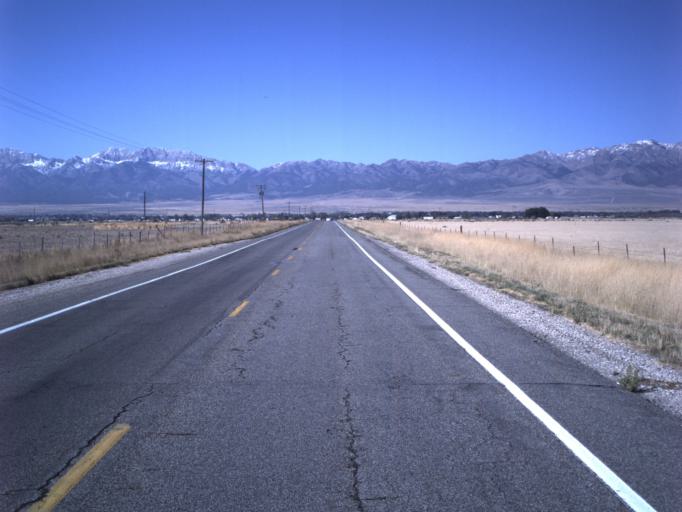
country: US
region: Utah
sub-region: Tooele County
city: Grantsville
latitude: 40.6041
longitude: -112.3947
